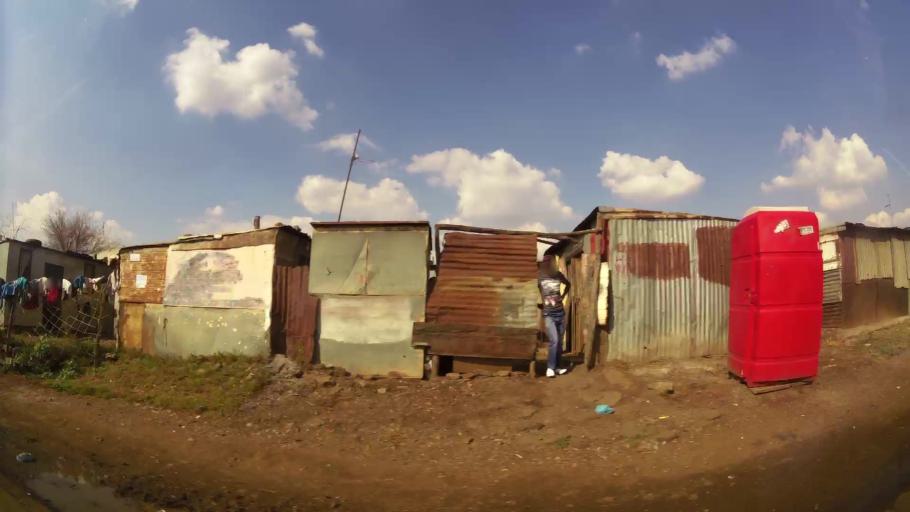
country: ZA
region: Gauteng
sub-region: Ekurhuleni Metropolitan Municipality
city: Germiston
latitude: -26.3320
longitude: 28.1405
